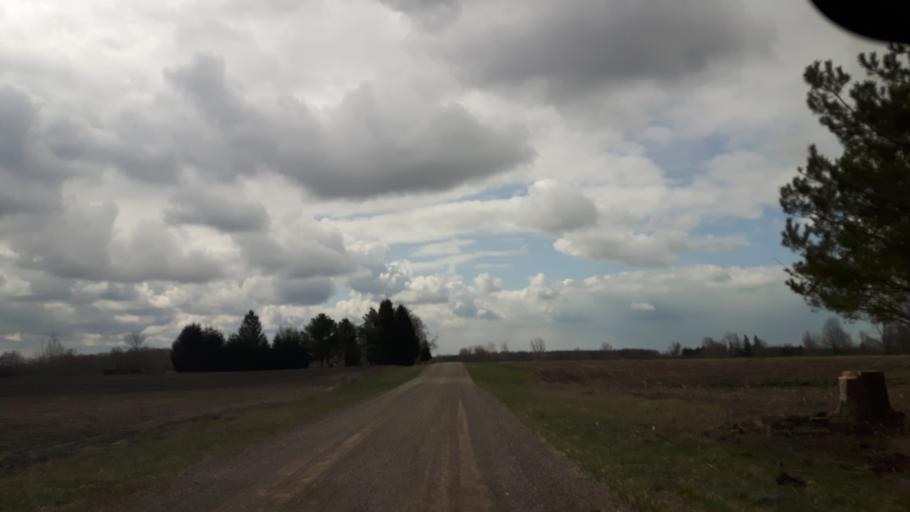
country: CA
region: Ontario
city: Bluewater
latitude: 43.5487
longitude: -81.6801
